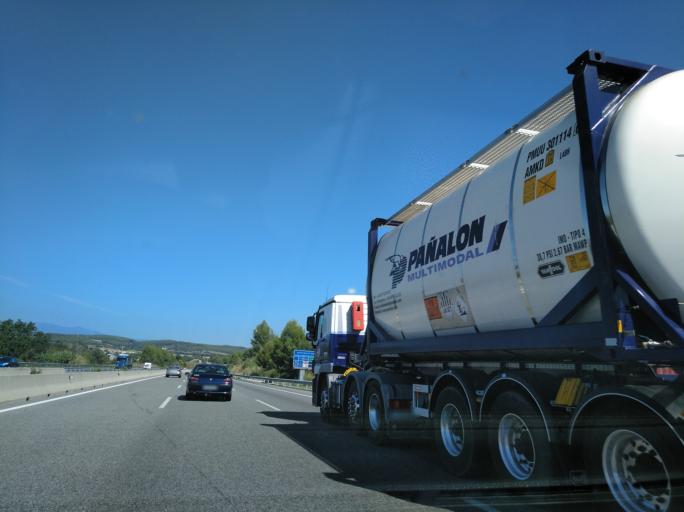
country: ES
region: Catalonia
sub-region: Provincia de Girona
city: Bascara
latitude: 42.1507
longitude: 2.9179
